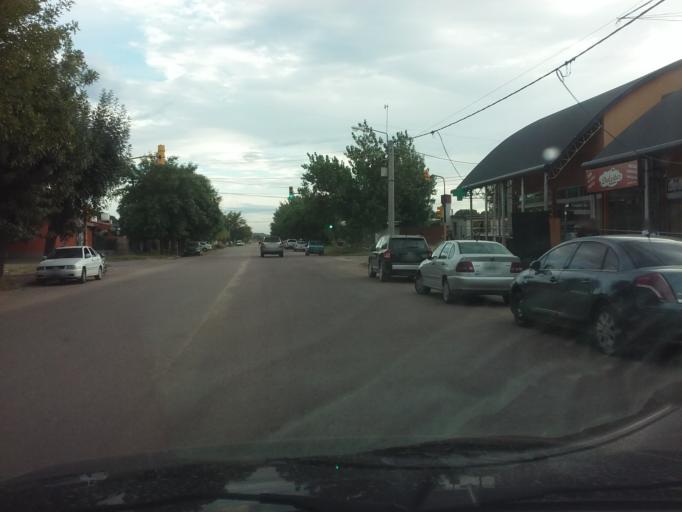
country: AR
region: La Pampa
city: Santa Rosa
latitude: -36.6437
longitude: -64.2942
